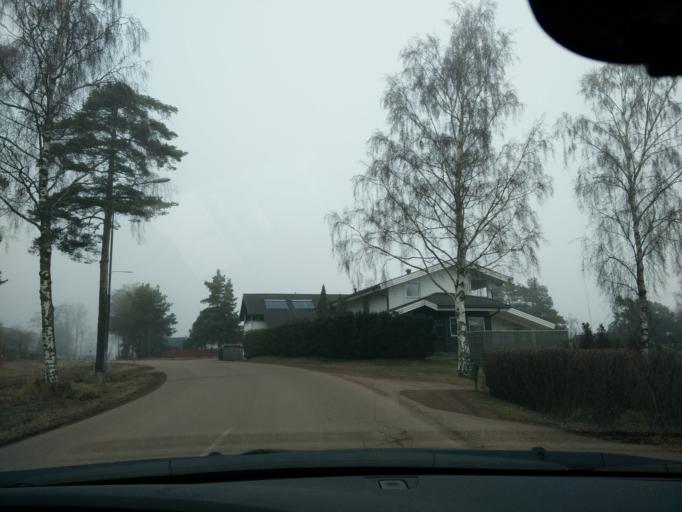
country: AX
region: Mariehamns stad
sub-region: Mariehamn
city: Mariehamn
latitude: 60.0820
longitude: 19.9600
